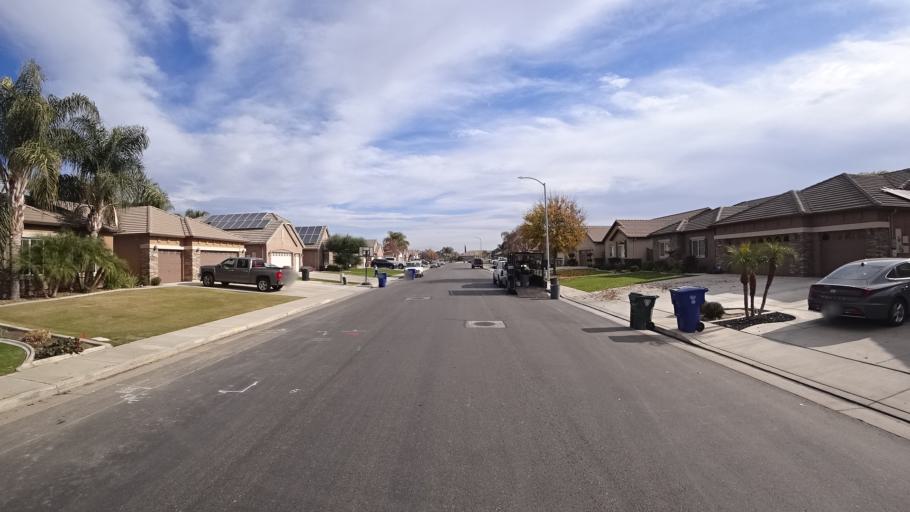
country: US
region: California
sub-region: Kern County
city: Rosedale
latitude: 35.4220
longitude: -119.1435
